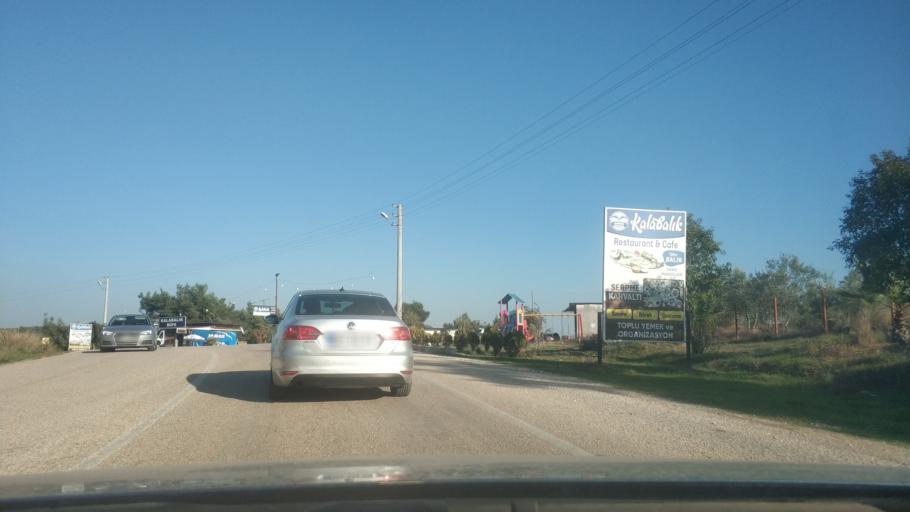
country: TR
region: Adana
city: Adana
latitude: 37.1031
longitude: 35.2939
